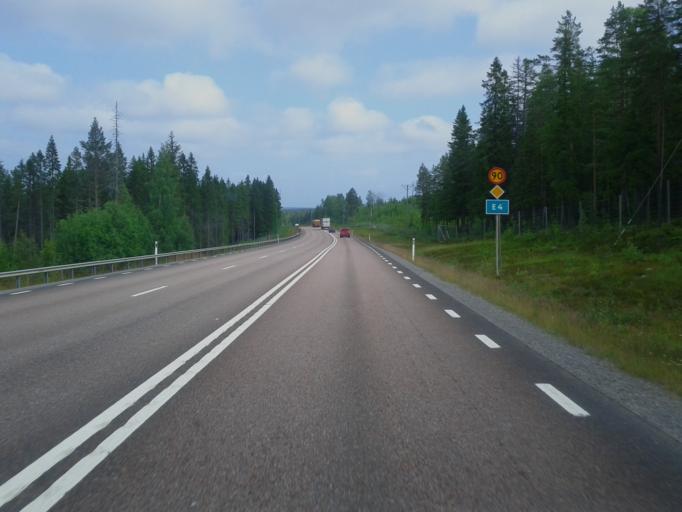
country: SE
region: Vaesterbotten
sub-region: Skelleftea Kommun
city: Burea
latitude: 64.4577
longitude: 21.2887
